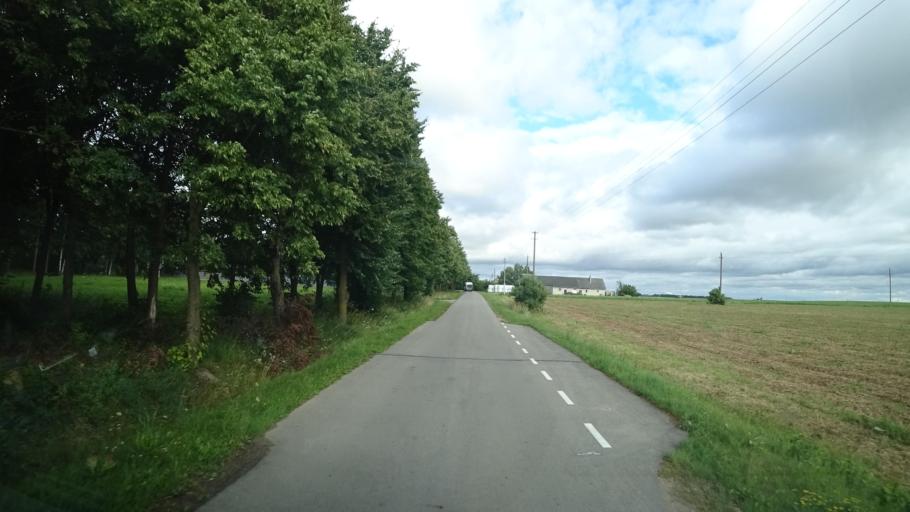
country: LT
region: Marijampoles apskritis
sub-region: Marijampole Municipality
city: Marijampole
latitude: 54.5189
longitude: 23.3310
